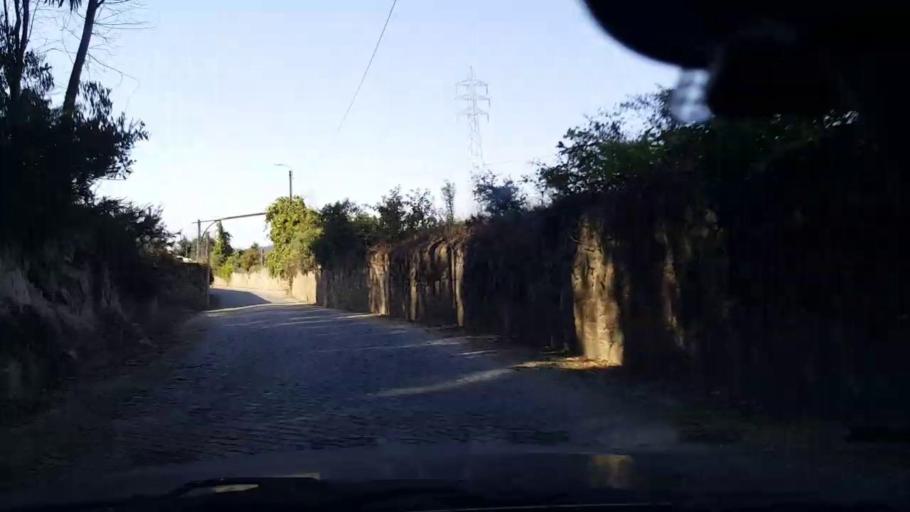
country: PT
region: Porto
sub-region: Vila do Conde
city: Arvore
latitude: 41.3568
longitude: -8.7088
